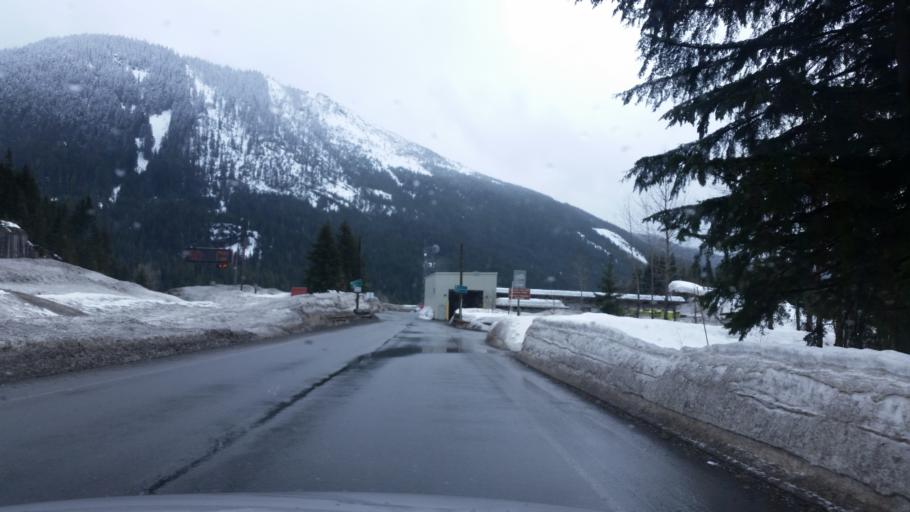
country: US
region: Washington
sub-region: King County
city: Tanner
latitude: 47.3930
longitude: -121.3907
